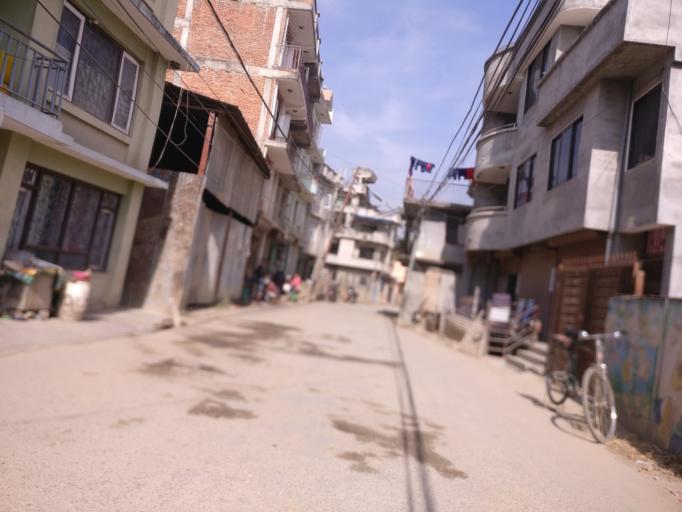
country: NP
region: Central Region
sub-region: Bagmati Zone
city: Patan
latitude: 27.6755
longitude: 85.3298
